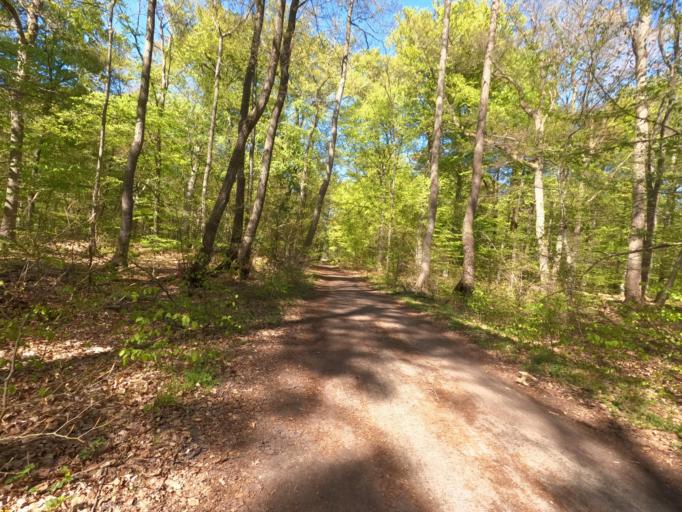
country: DE
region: Mecklenburg-Vorpommern
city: Ostseebad Prerow
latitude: 54.4483
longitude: 12.5456
